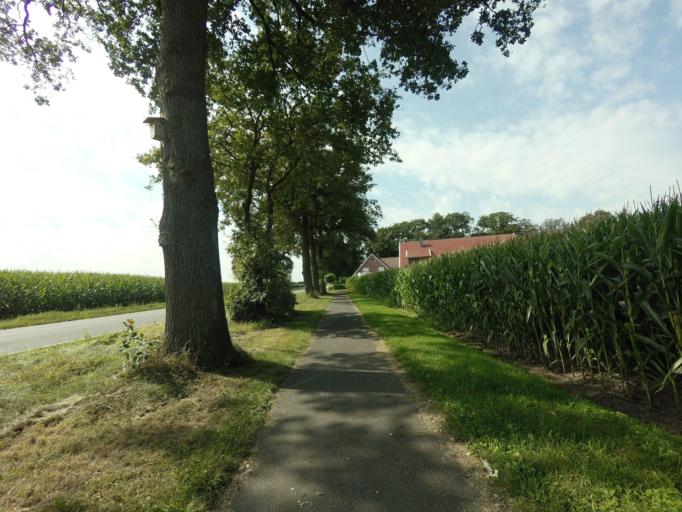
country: DE
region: Lower Saxony
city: Itterbeck
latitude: 52.5364
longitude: 6.7673
